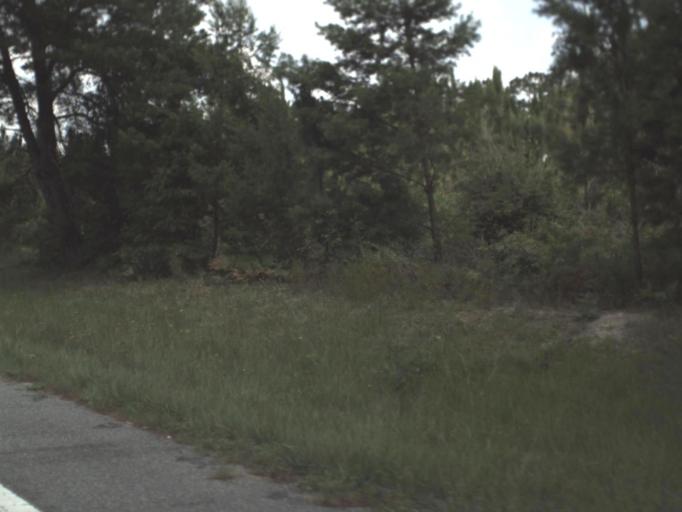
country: US
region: Florida
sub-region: Madison County
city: Madison
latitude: 30.4867
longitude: -83.1840
